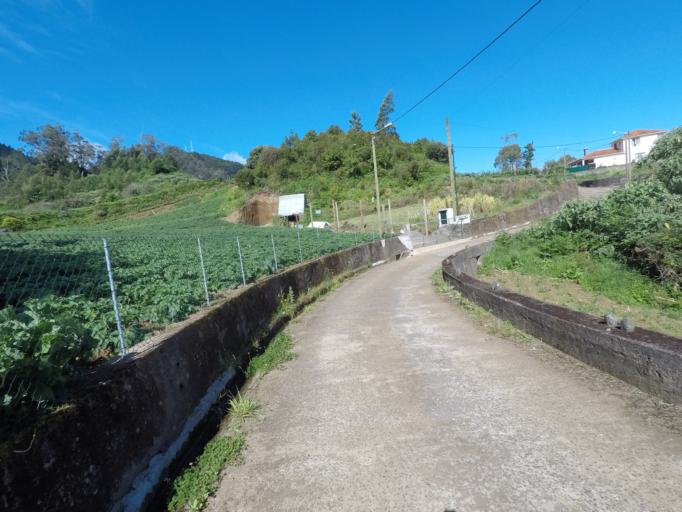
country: PT
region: Madeira
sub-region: Santana
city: Santana
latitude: 32.8217
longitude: -16.9395
